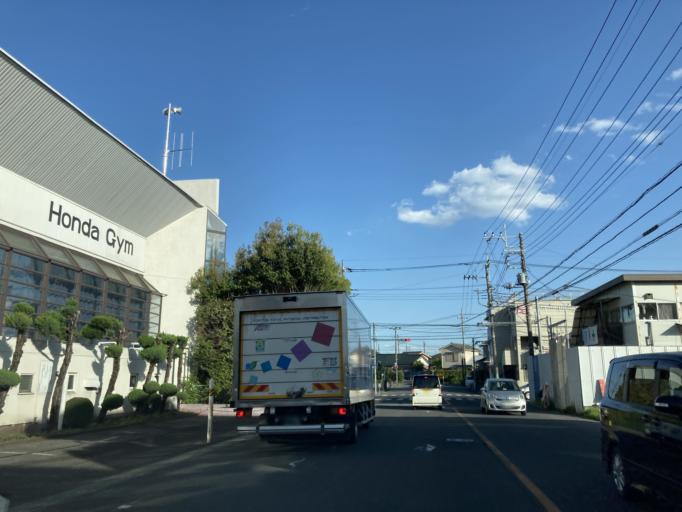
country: JP
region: Saitama
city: Sayama
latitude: 35.8734
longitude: 139.4386
